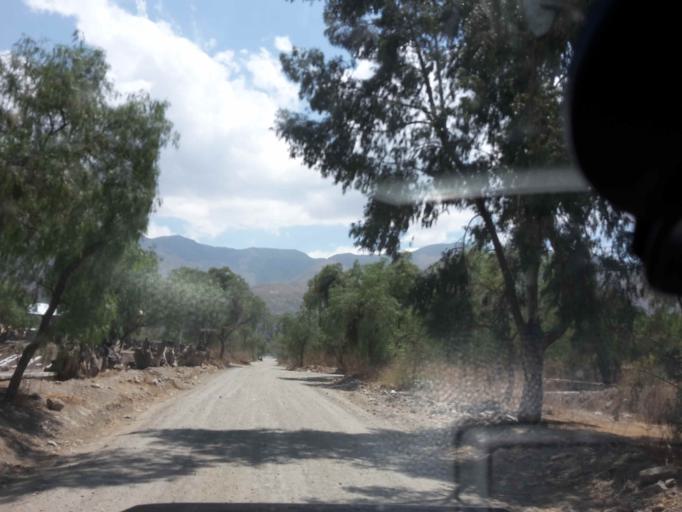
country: BO
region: Cochabamba
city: Cochabamba
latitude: -17.3402
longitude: -66.2122
